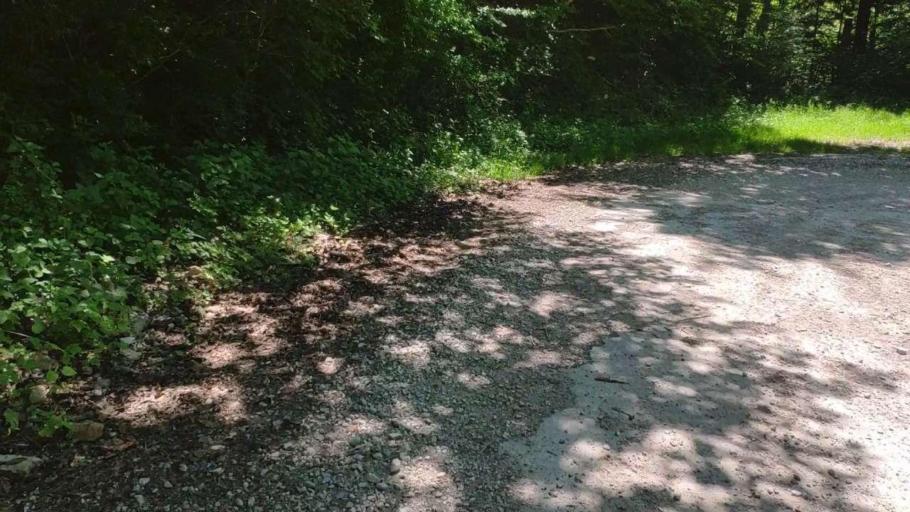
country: FR
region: Franche-Comte
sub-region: Departement du Jura
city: Perrigny
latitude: 46.7317
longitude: 5.6563
